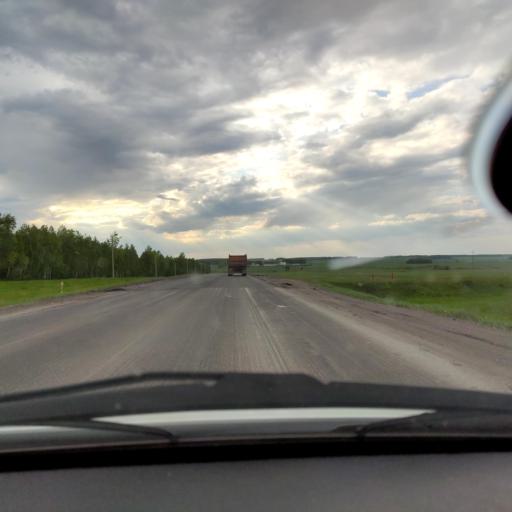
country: RU
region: Bashkortostan
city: Dyurtyuli
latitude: 55.3414
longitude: 54.9397
